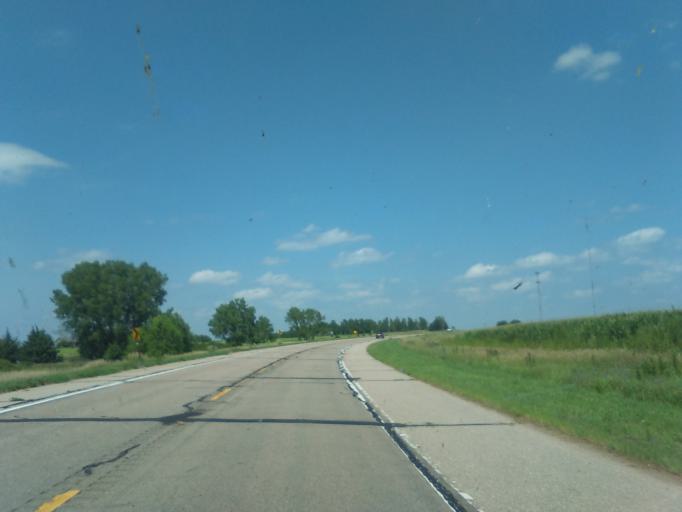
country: US
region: Nebraska
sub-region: Dawson County
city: Lexington
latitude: 40.6961
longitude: -99.7939
